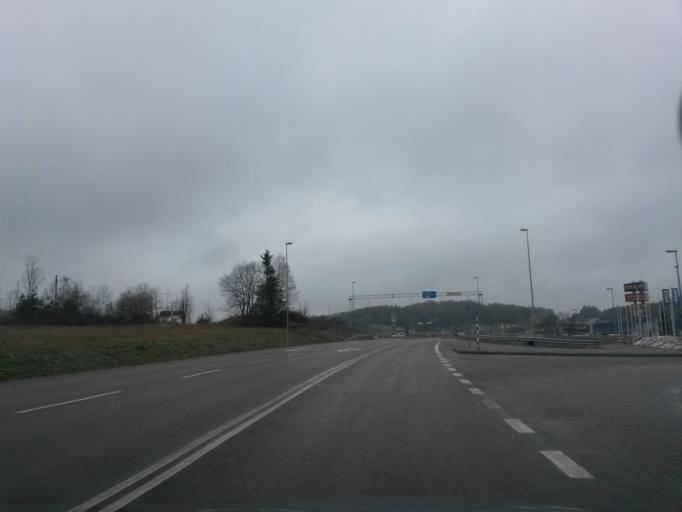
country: SE
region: Vaestra Goetaland
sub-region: Uddevalla Kommun
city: Uddevalla
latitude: 58.3517
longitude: 11.8246
